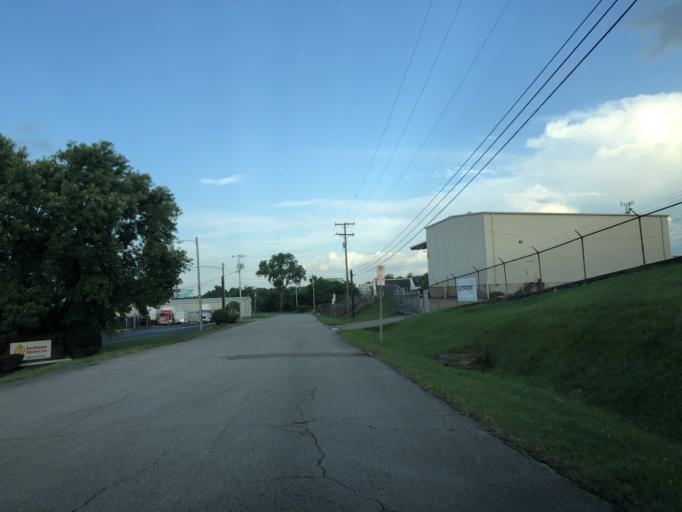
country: US
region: Tennessee
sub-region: Davidson County
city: Nashville
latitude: 36.1416
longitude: -86.7265
